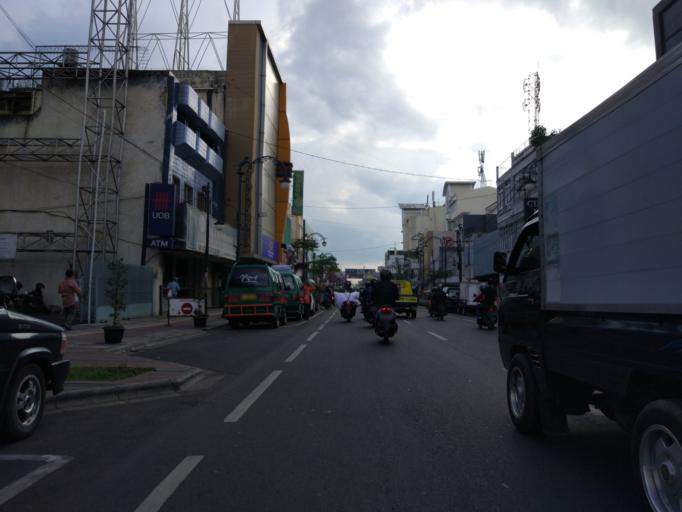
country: ID
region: West Java
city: Bandung
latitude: -6.9207
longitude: 107.6028
